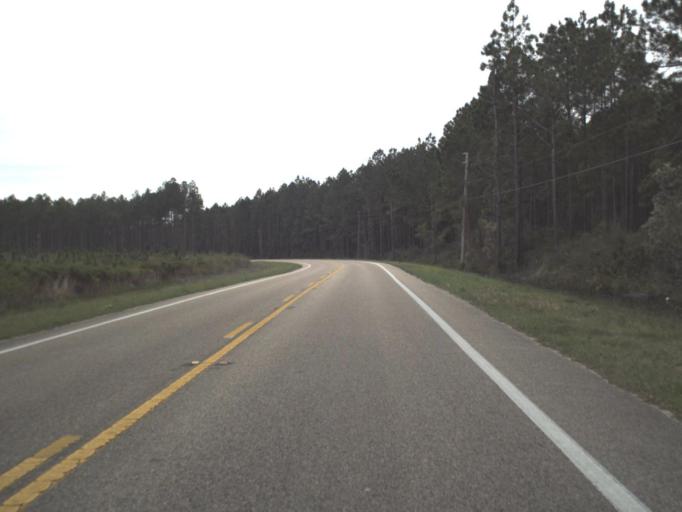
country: US
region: Florida
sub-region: Gulf County
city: Port Saint Joe
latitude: 29.8380
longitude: -85.2725
